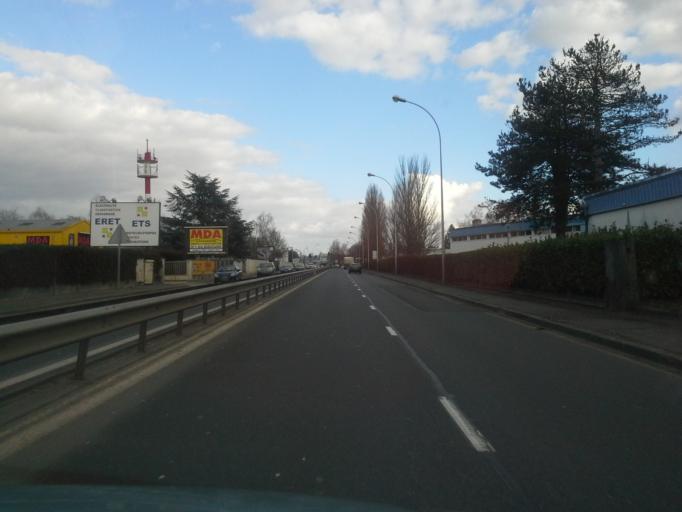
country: FR
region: Centre
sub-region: Departement d'Indre-et-Loire
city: Saint-Cyr-sur-Loire
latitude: 47.4304
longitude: 0.6746
